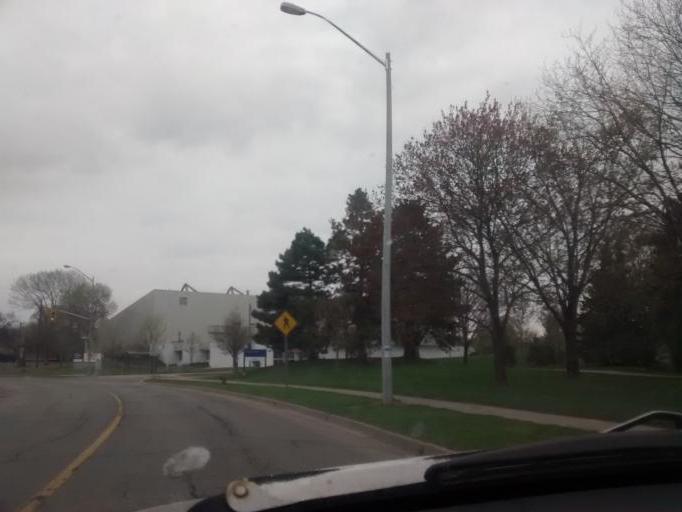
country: CA
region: Ontario
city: Burlington
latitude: 43.3342
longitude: -79.7928
